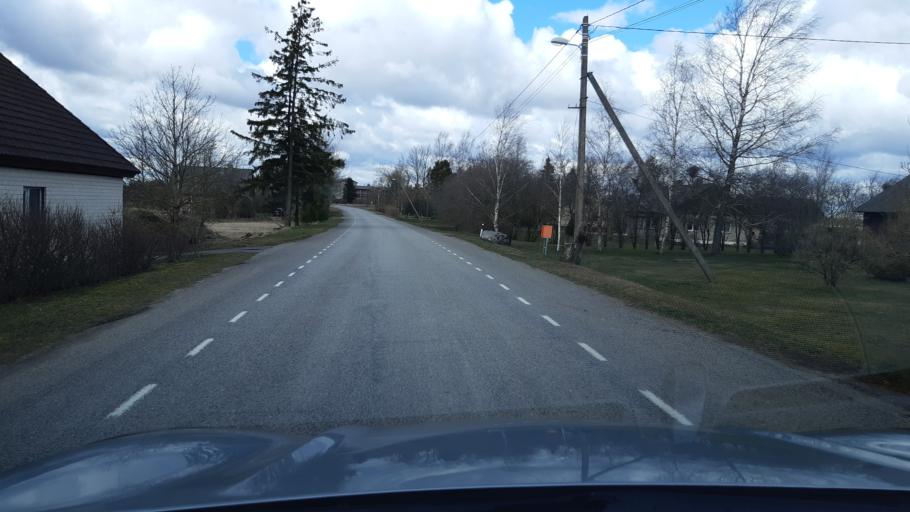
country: EE
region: Raplamaa
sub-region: Kehtna vald
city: Kehtna
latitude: 59.0392
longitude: 25.1293
